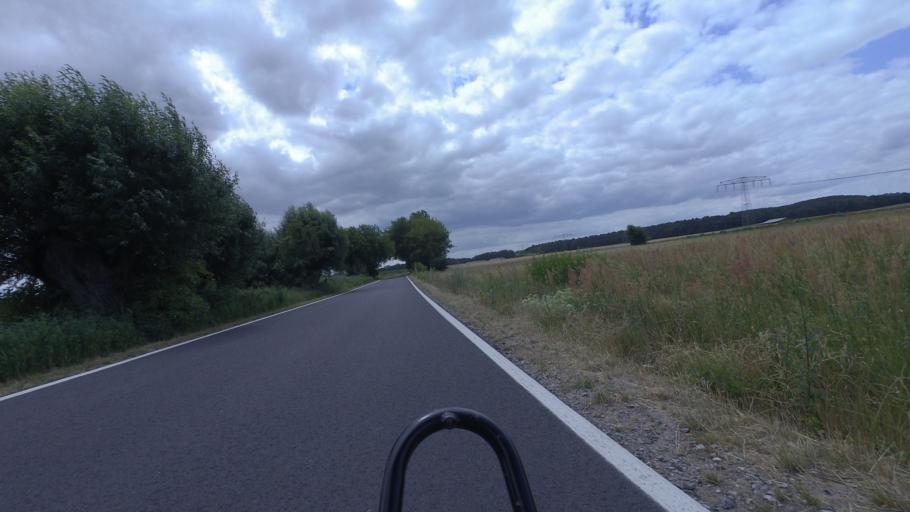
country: DE
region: Brandenburg
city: Ludwigsfelde
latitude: 52.2574
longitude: 13.3026
